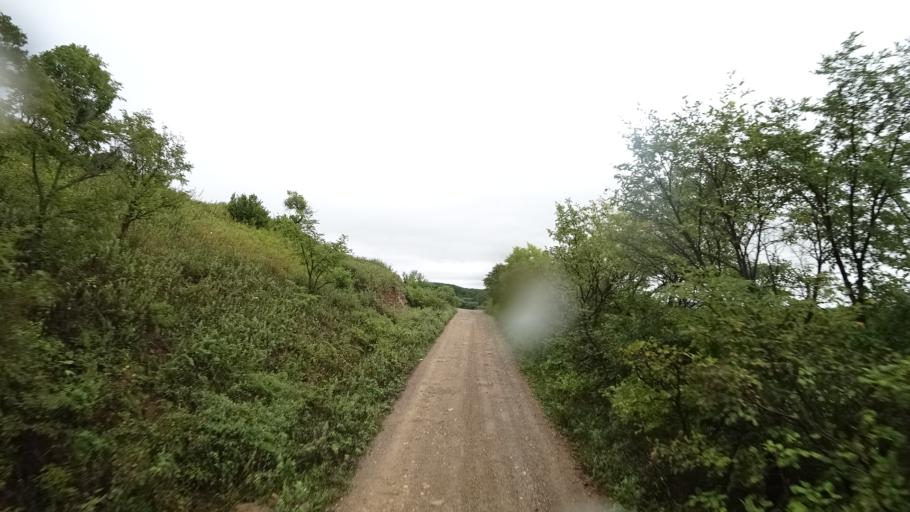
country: RU
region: Primorskiy
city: Monastyrishche
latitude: 44.2595
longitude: 132.4082
